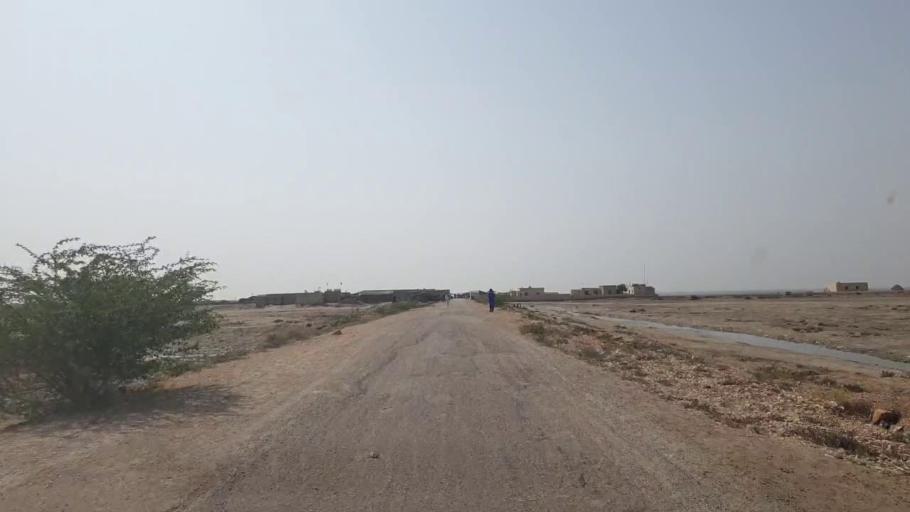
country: PK
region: Sindh
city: Jati
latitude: 24.3383
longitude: 68.5931
